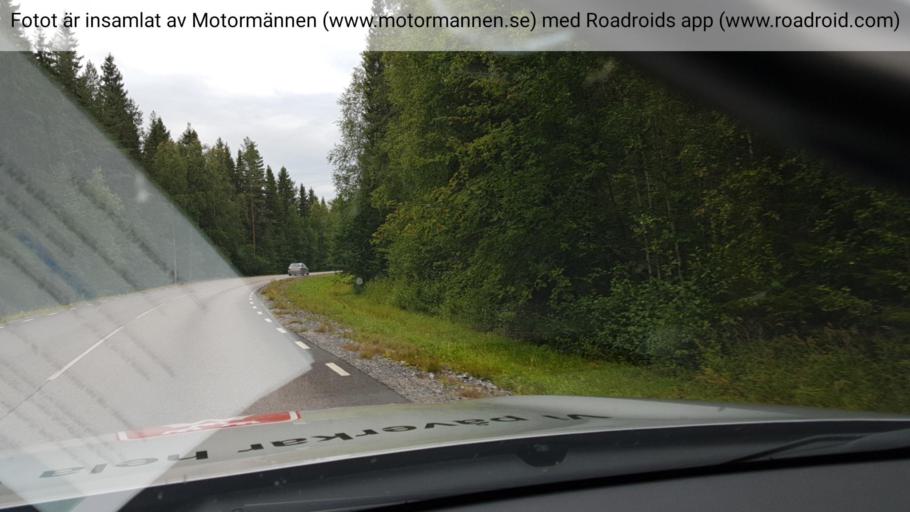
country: SE
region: Norrbotten
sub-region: Lulea Kommun
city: Gammelstad
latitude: 65.6568
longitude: 22.0498
